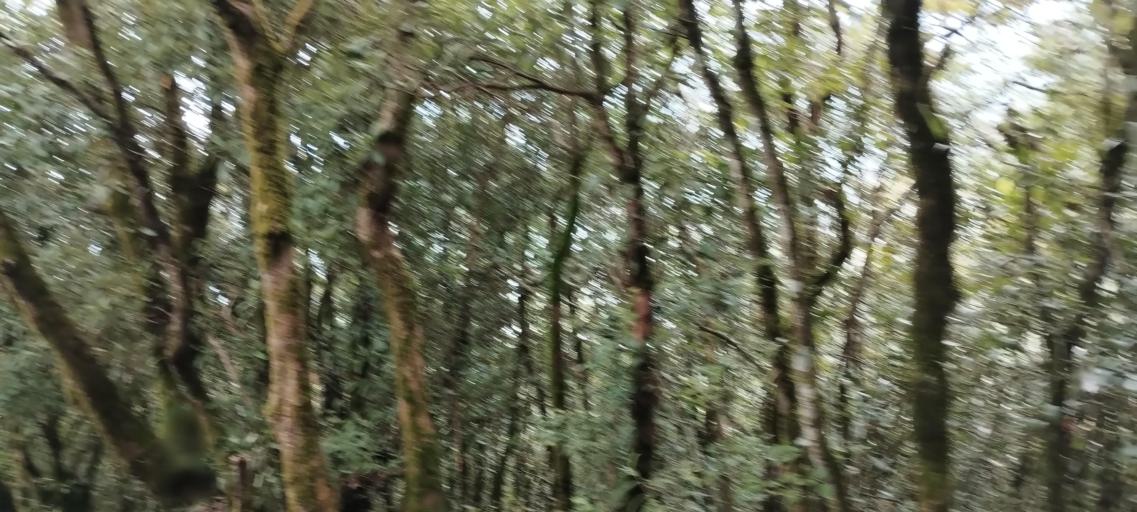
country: NP
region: Central Region
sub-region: Bagmati Zone
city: Kathmandu
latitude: 27.7883
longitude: 85.3810
